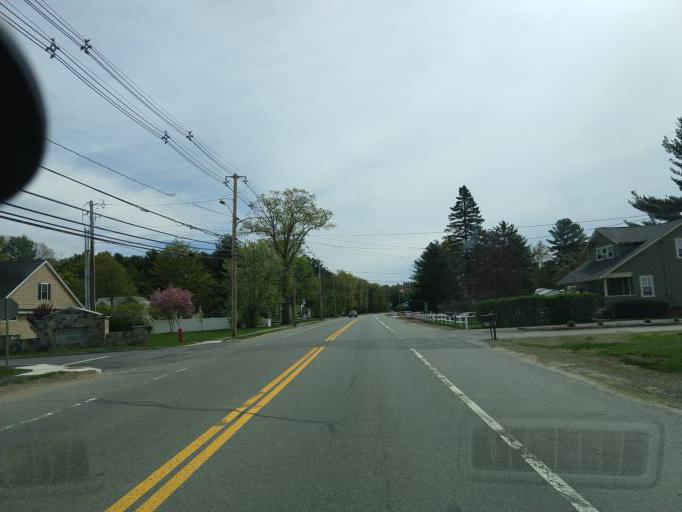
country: US
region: Massachusetts
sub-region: Essex County
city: Merrimac
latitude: 42.8378
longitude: -70.9874
